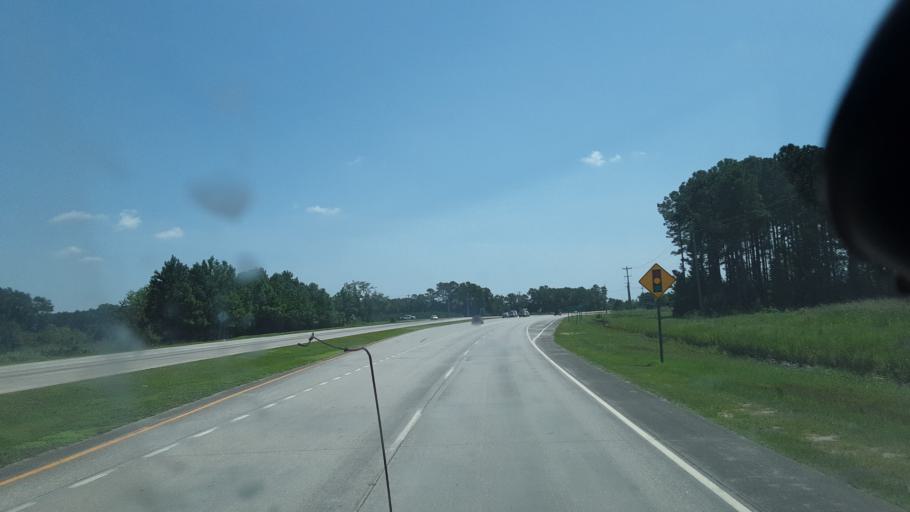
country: US
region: South Carolina
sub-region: Horry County
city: North Myrtle Beach
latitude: 33.8527
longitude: -78.7076
